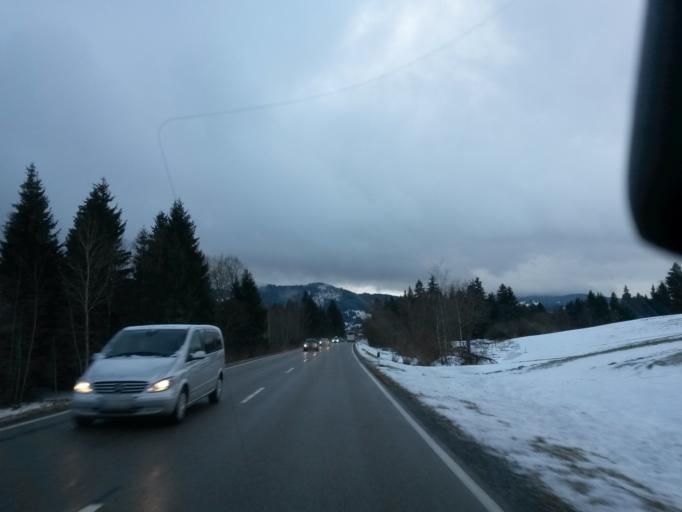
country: DE
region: Bavaria
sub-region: Swabia
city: Wertach
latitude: 47.6096
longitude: 10.4300
